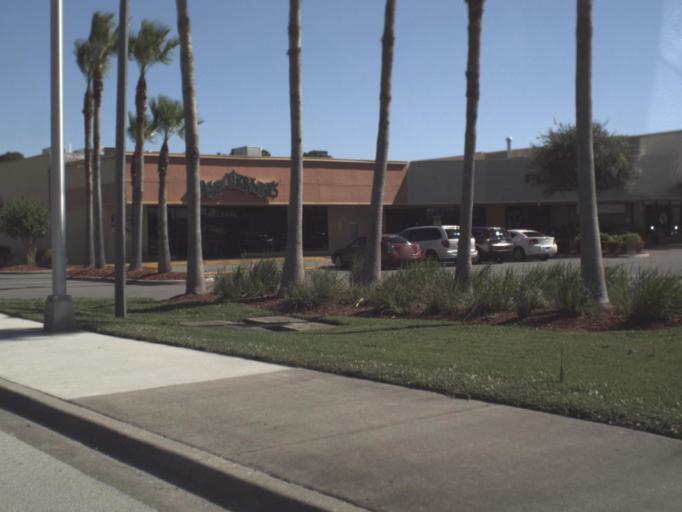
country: US
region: Florida
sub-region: Charlotte County
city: Manasota Key
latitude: 26.9376
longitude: -82.3351
